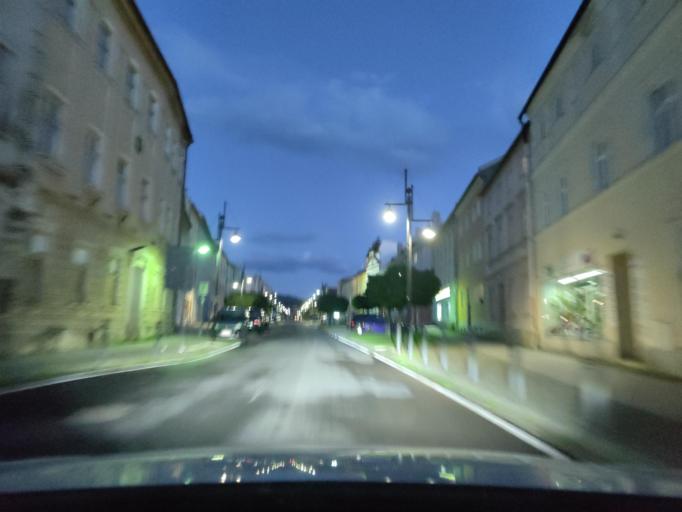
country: CZ
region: Olomoucky
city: Zlate Hory
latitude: 50.2651
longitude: 17.3957
